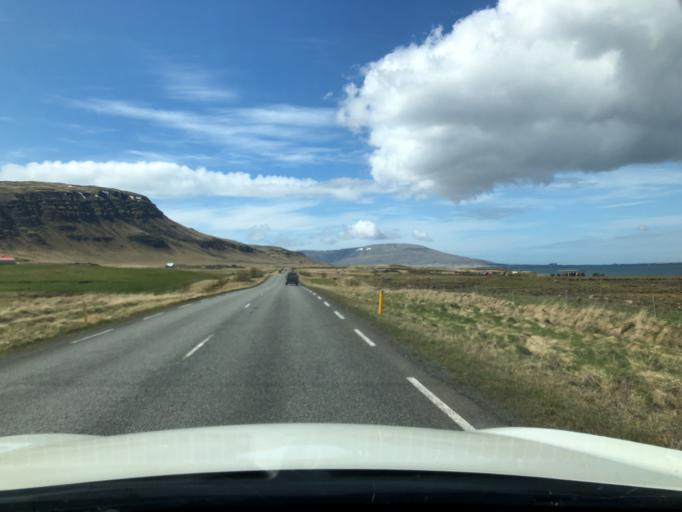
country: IS
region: Capital Region
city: Mosfellsbaer
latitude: 64.3302
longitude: -21.6439
